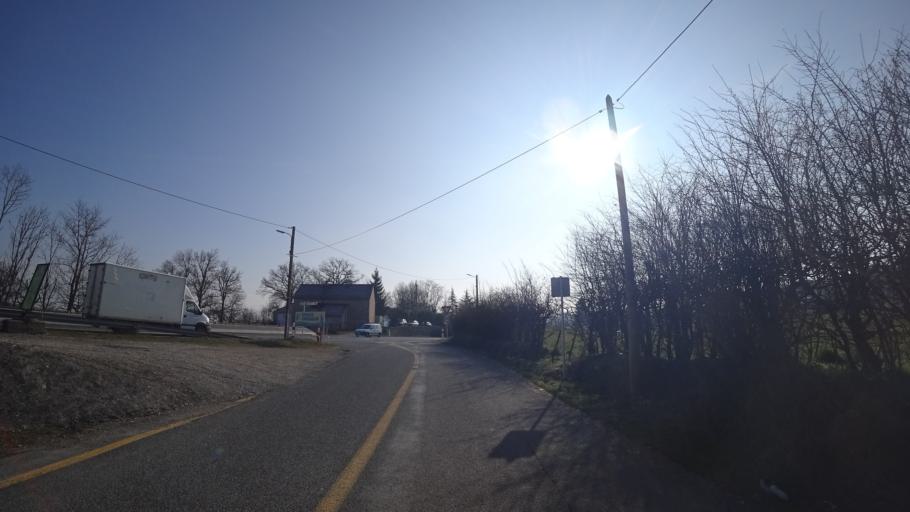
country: FR
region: Midi-Pyrenees
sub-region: Departement de l'Aveyron
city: Olemps
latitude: 44.3655
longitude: 2.5506
